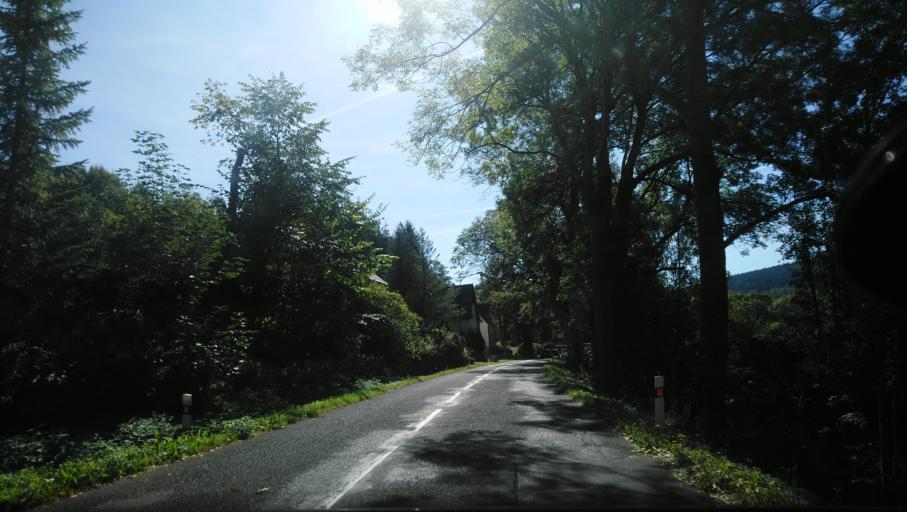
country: CZ
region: Ustecky
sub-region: Okres Chomutov
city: Vejprty
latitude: 50.4735
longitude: 13.0212
